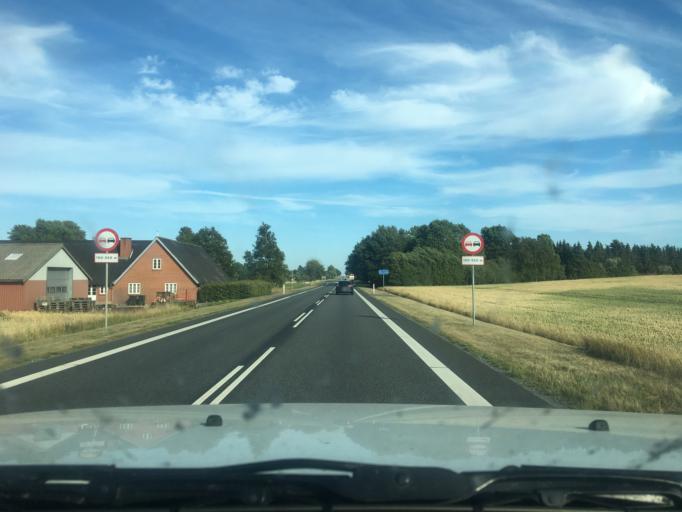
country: DK
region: Central Jutland
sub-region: Syddjurs Kommune
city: Hornslet
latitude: 56.3852
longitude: 10.2864
